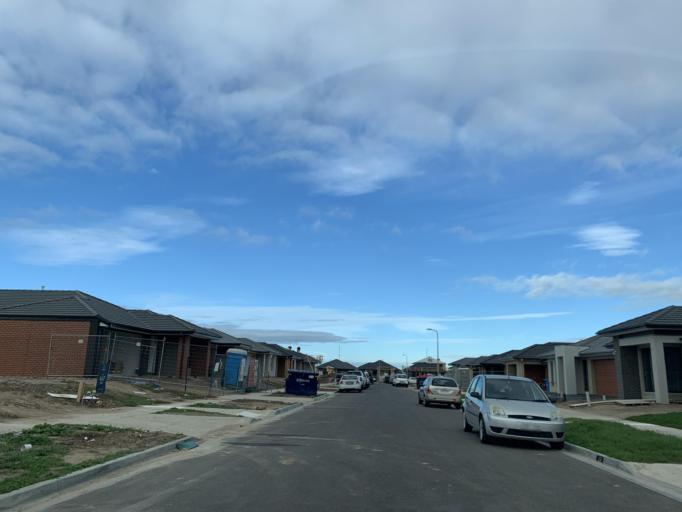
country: AU
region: Victoria
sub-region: Cardinia
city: Officer South
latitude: -38.1223
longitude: 145.3735
